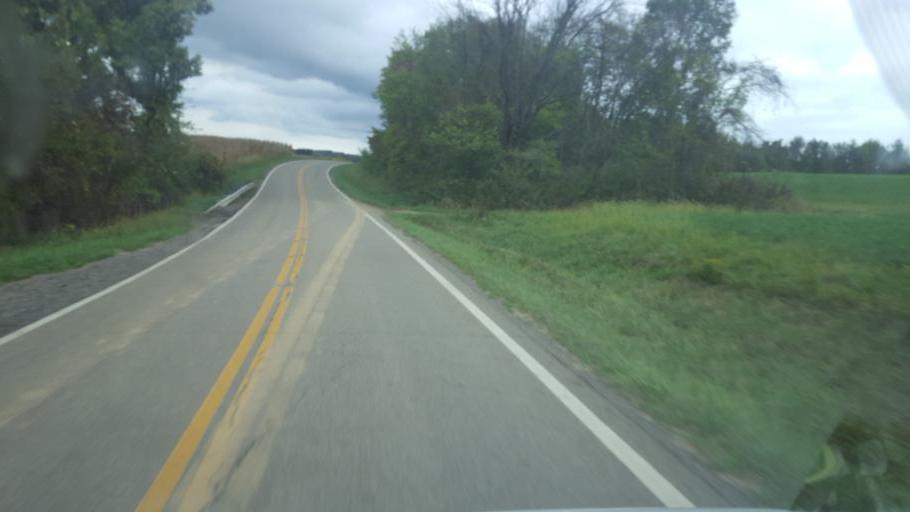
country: US
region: Ohio
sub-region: Ashland County
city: Loudonville
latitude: 40.5361
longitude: -82.1567
